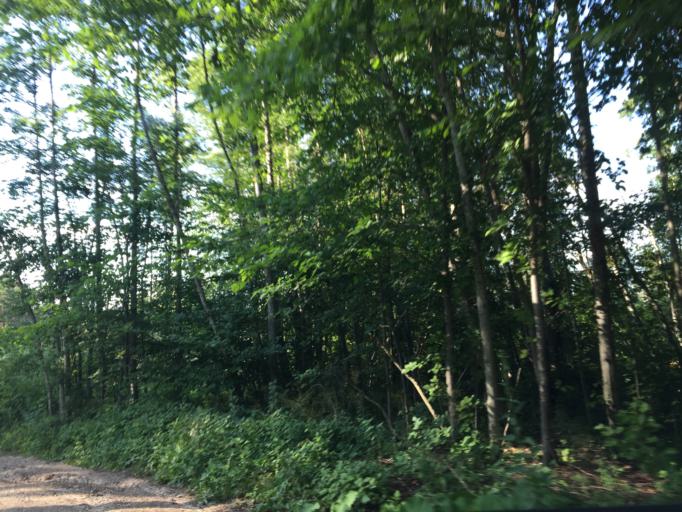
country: LV
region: Krimulda
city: Ragana
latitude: 57.1431
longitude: 24.7647
